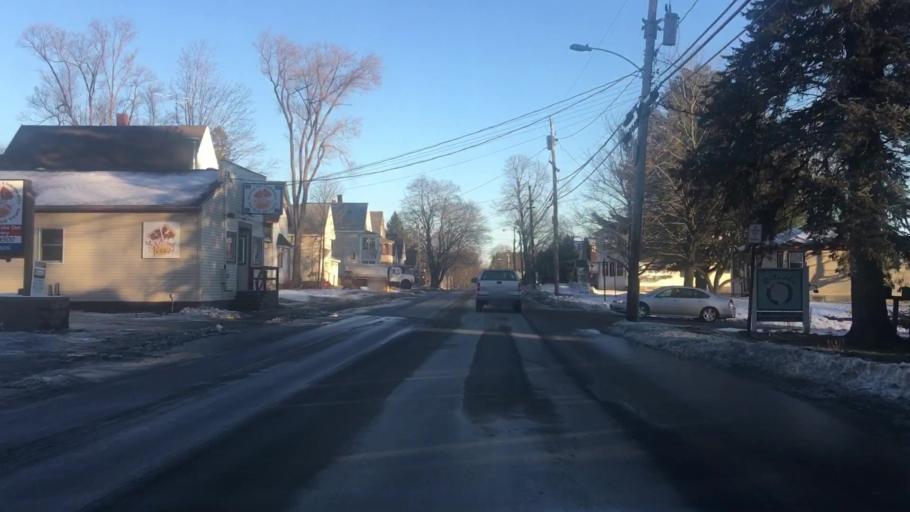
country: US
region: Maine
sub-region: Kennebec County
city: Winslow
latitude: 44.5464
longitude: -69.6192
